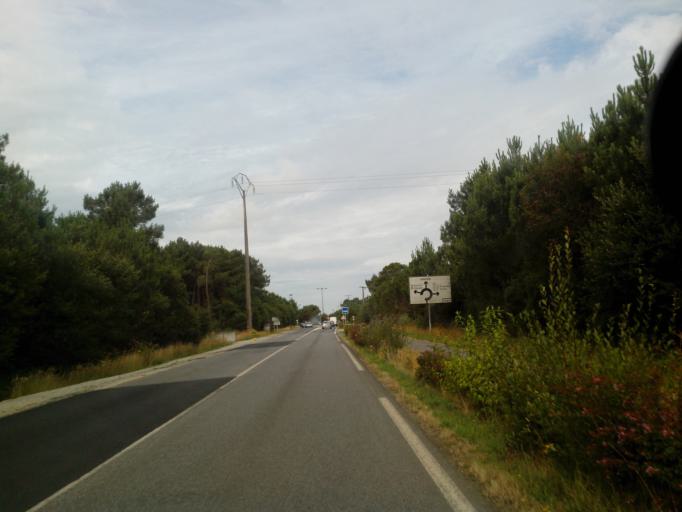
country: FR
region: Brittany
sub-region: Departement du Morbihan
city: Ploemel
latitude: 47.6428
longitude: -3.1074
